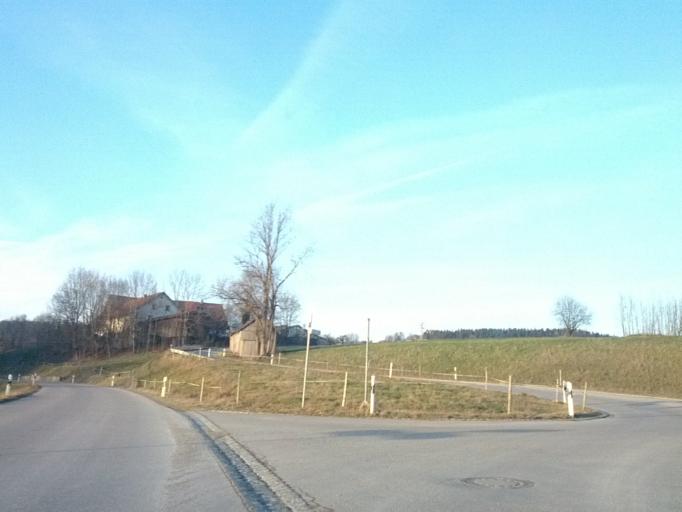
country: DE
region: Bavaria
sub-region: Swabia
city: Kronburg
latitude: 47.8902
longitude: 10.1610
